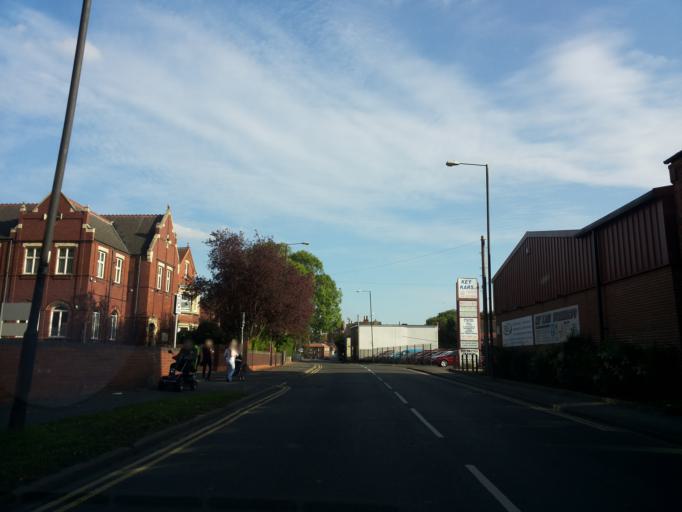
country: GB
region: England
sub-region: Doncaster
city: Hatfield
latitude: 53.6140
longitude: -0.9688
